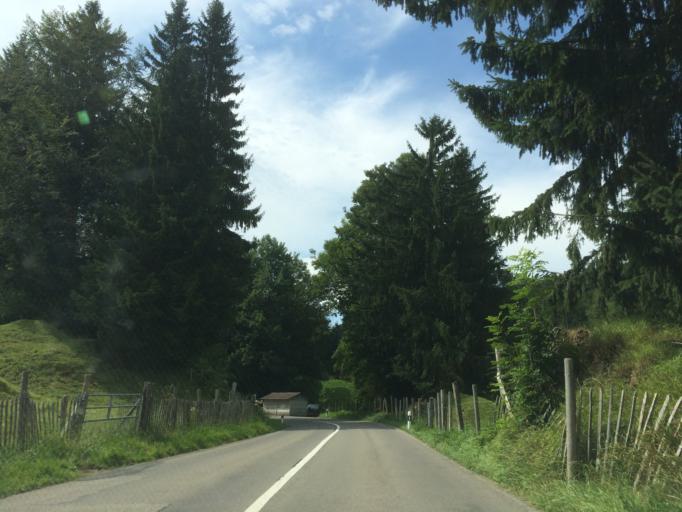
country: CH
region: Saint Gallen
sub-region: Wahlkreis Toggenburg
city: Krummenau
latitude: 47.2431
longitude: 9.2288
